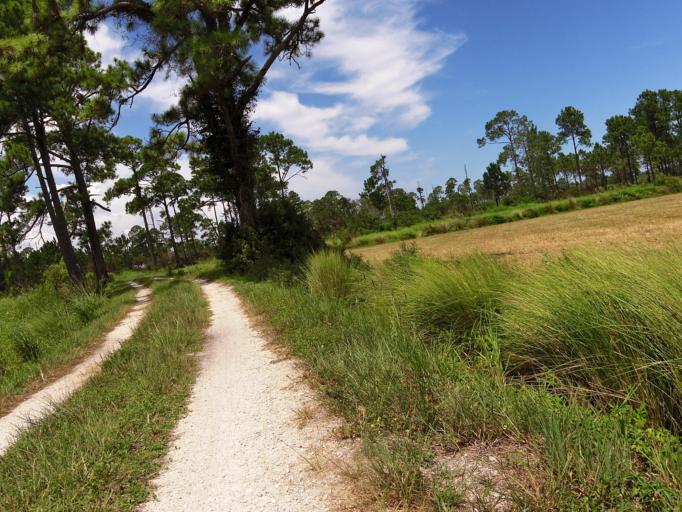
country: US
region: Florida
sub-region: Saint Johns County
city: Villano Beach
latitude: 30.0363
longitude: -81.3422
